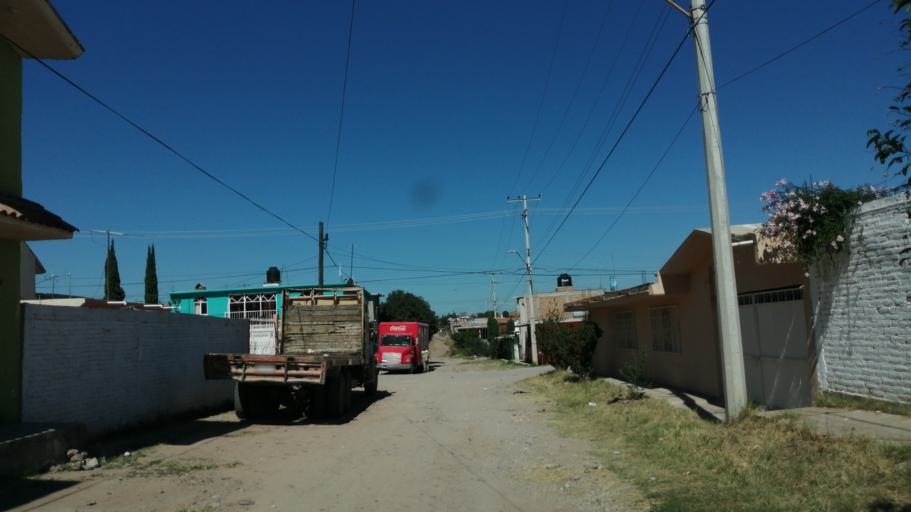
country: MX
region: Durango
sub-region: Santiago Papasquiaro
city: Santiago Papasquiaro
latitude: 25.0501
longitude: -105.4361
